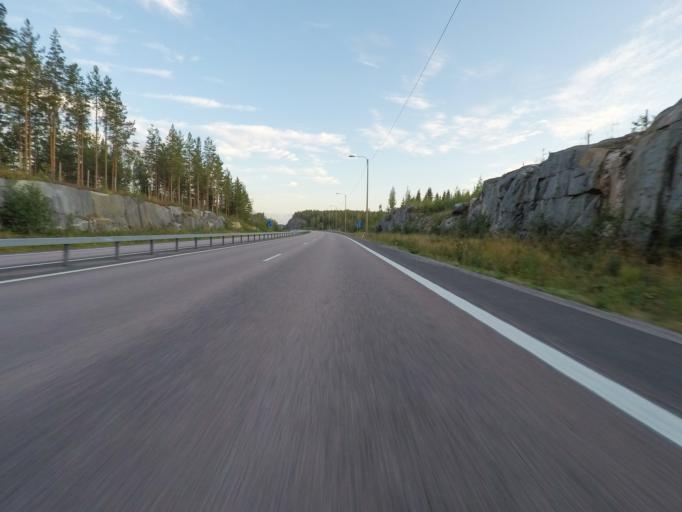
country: FI
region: Central Finland
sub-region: Jyvaeskylae
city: Saeynaetsalo
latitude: 62.2135
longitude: 25.8901
